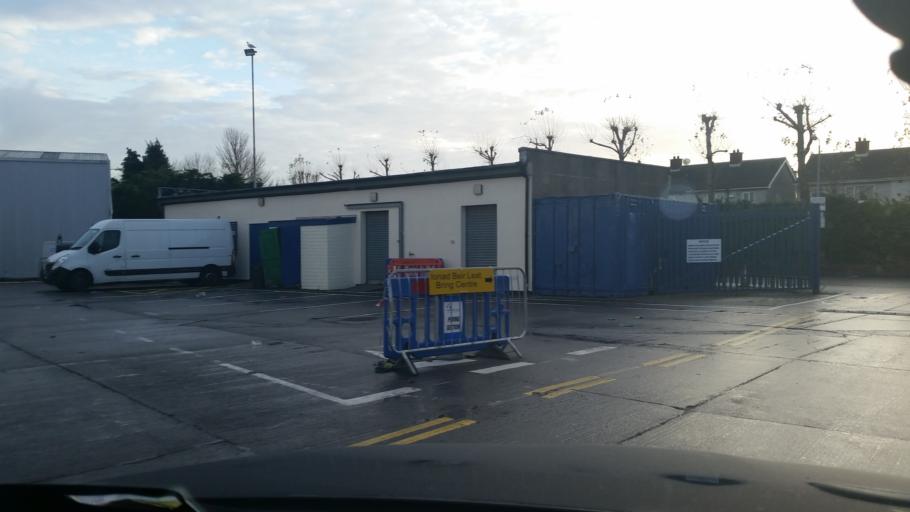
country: IE
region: Leinster
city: Glasnevin
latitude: 53.3874
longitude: -6.2541
